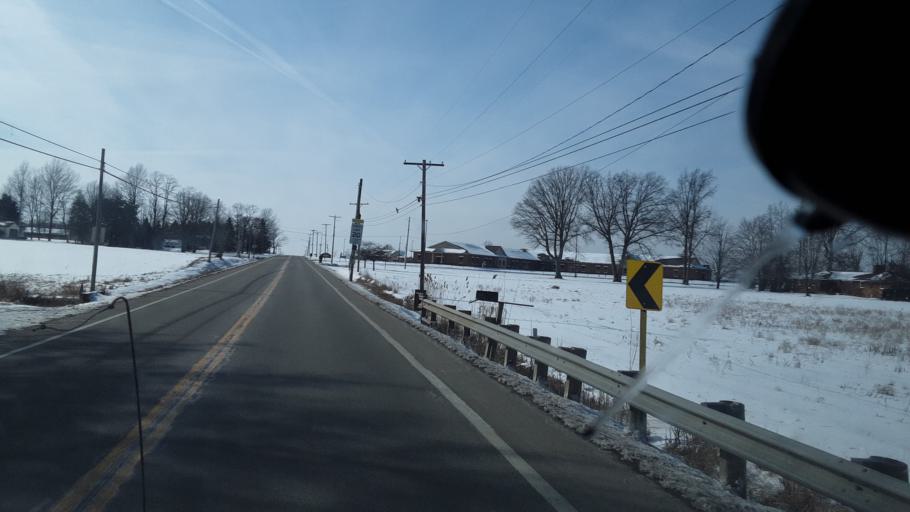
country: US
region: Ohio
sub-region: Mahoning County
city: Craig Beach
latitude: 41.0246
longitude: -80.9087
